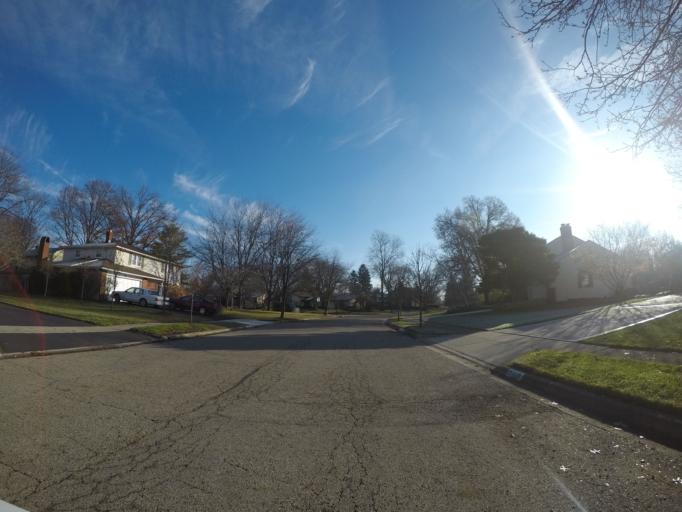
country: US
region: Ohio
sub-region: Franklin County
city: Upper Arlington
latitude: 40.0459
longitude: -83.0758
